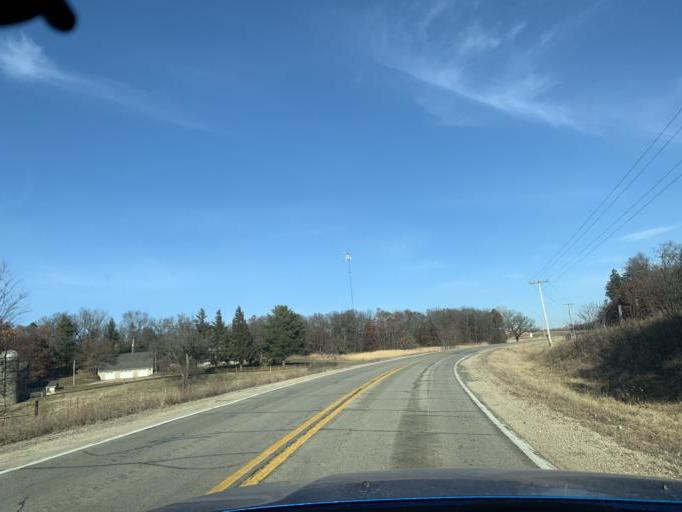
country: US
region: Wisconsin
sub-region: Green County
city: New Glarus
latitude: 42.7904
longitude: -89.8601
